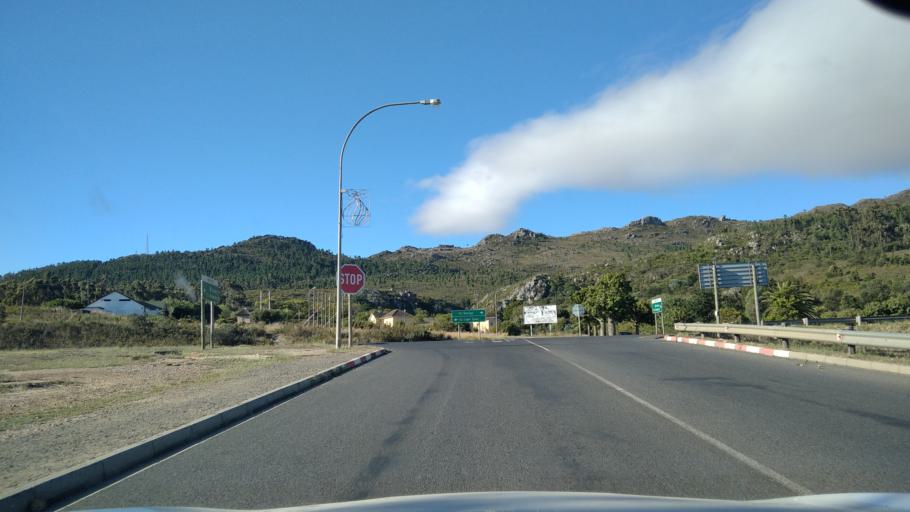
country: ZA
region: Western Cape
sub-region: Overberg District Municipality
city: Caledon
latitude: -34.2279
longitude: 19.4290
